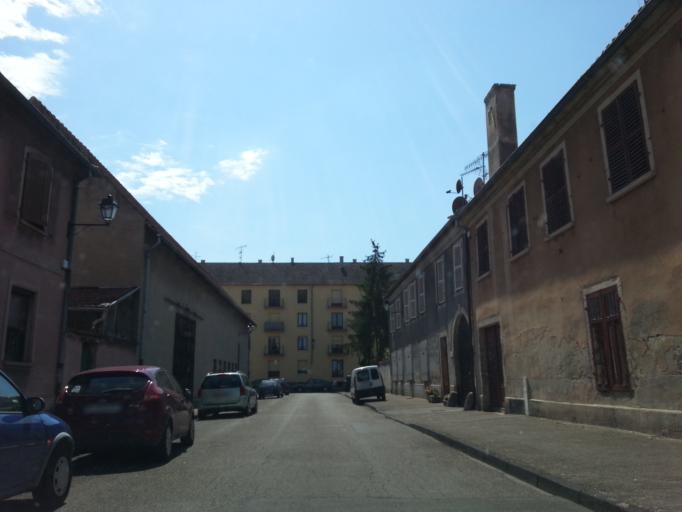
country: FR
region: Alsace
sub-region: Departement du Haut-Rhin
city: Neuf-Brisach
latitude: 48.0168
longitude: 7.5260
